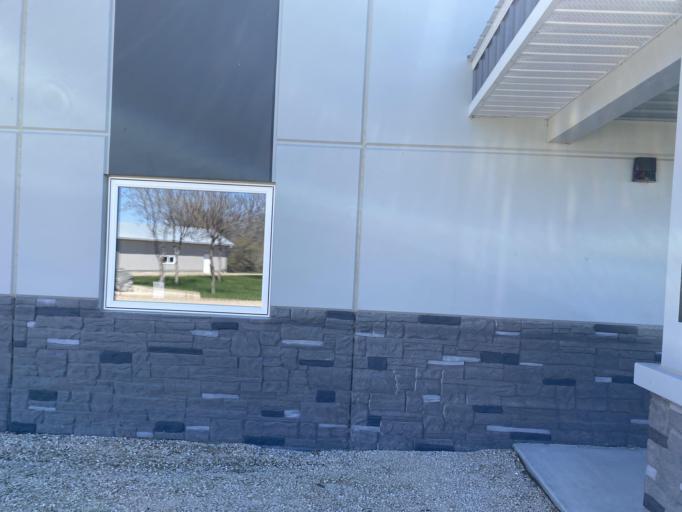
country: CA
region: Manitoba
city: Portage la Prairie
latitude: 50.1419
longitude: -98.6768
